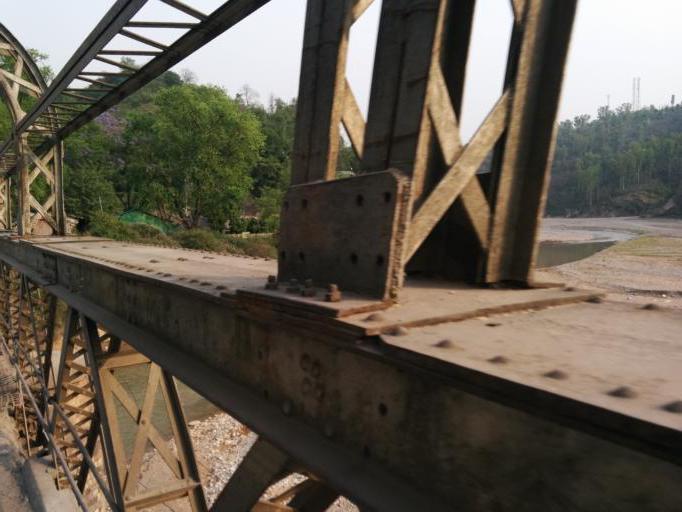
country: IN
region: Himachal Pradesh
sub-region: Kangra
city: Kotla
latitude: 32.2376
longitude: 76.0471
